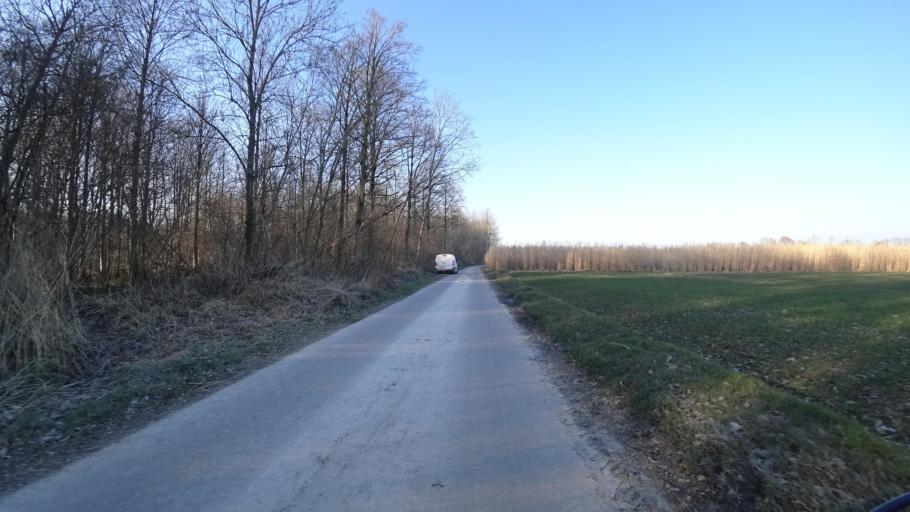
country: BE
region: Wallonia
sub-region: Province du Brabant Wallon
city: Walhain-Saint-Paul
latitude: 50.6311
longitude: 4.7439
